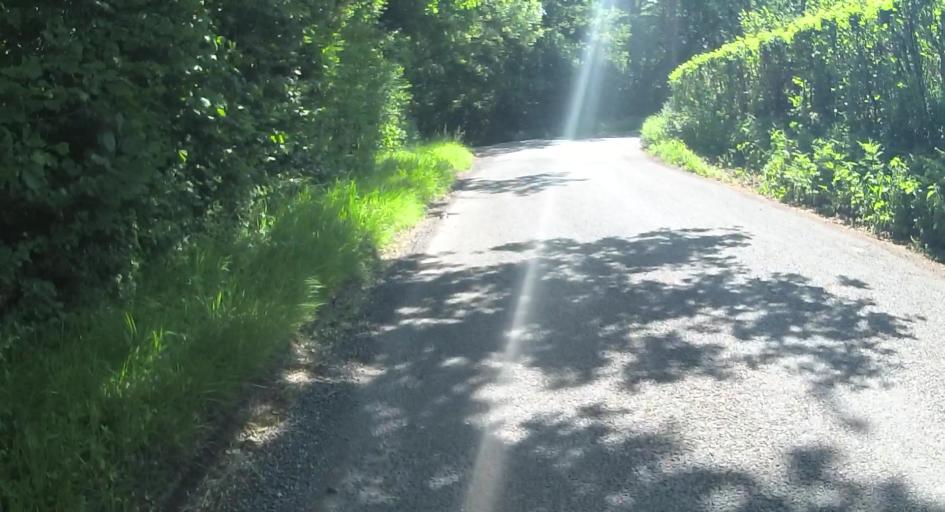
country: GB
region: England
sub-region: West Berkshire
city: Greenham
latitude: 51.3624
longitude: -1.2770
